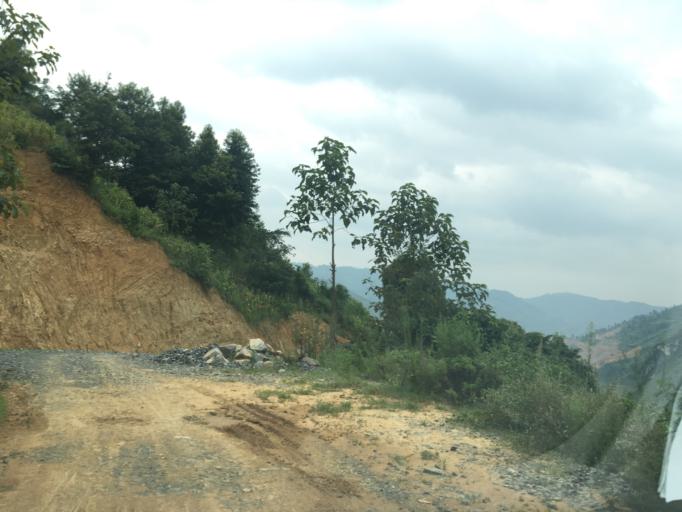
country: CN
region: Guangxi Zhuangzu Zizhiqu
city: Xinzhou
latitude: 25.1738
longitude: 105.7320
